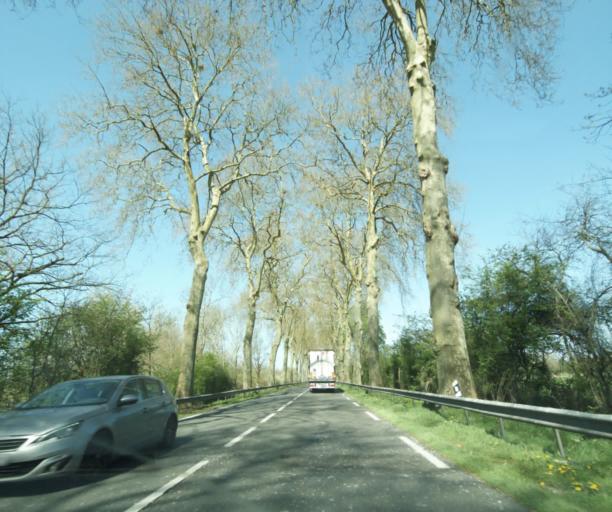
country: FR
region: Bourgogne
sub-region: Departement de la Nievre
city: Chantenay-Saint-Imbert
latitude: 46.7229
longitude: 3.1796
